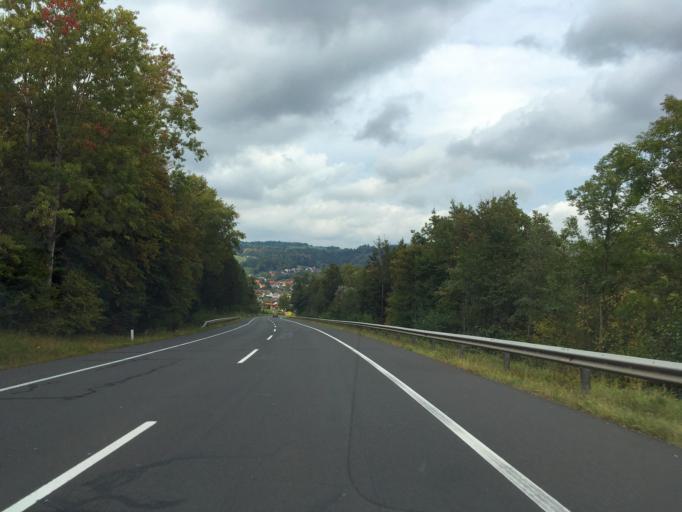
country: AT
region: Styria
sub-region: Politischer Bezirk Hartberg-Fuerstenfeld
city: Pinggau
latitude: 47.4330
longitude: 16.0653
